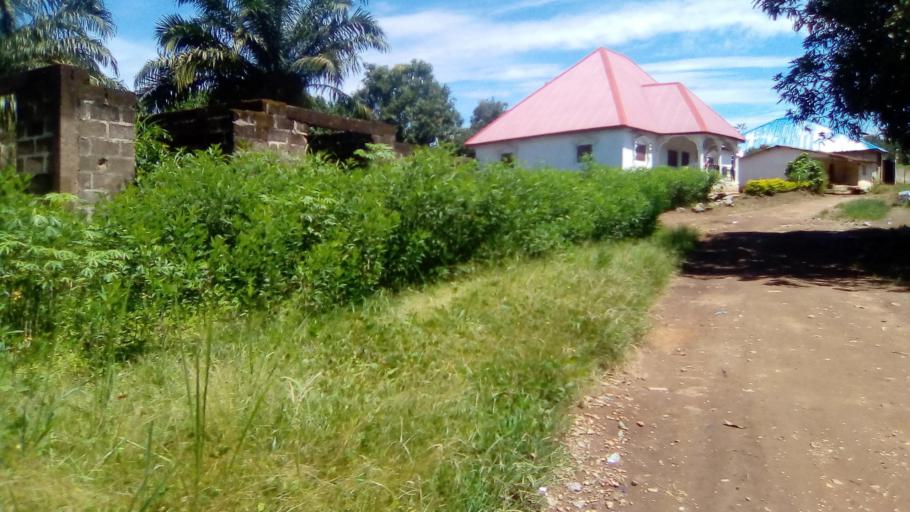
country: SL
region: Eastern Province
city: Simbakoro
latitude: 8.6296
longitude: -10.9949
